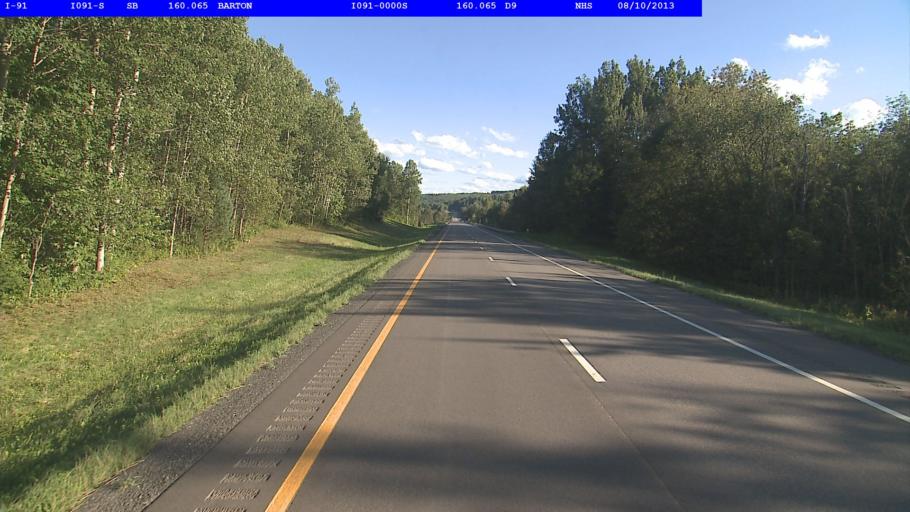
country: US
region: Vermont
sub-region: Orleans County
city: Newport
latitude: 44.7874
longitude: -72.2162
